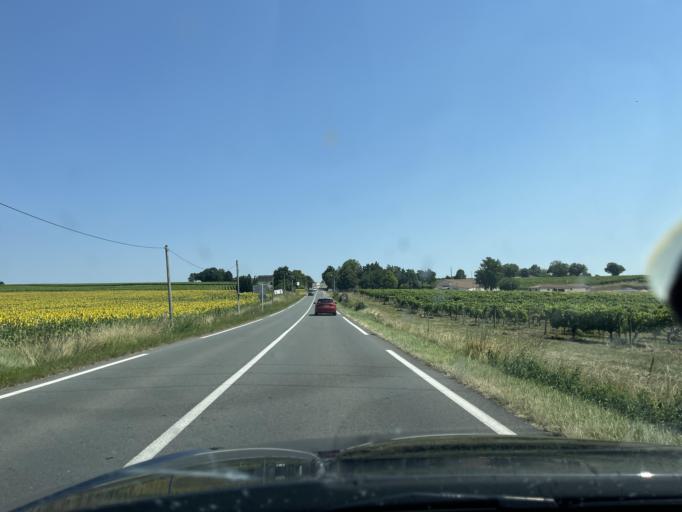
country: FR
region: Poitou-Charentes
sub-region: Departement de la Charente-Maritime
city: Mortagne-sur-Gironde
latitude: 45.4621
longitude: -0.6988
